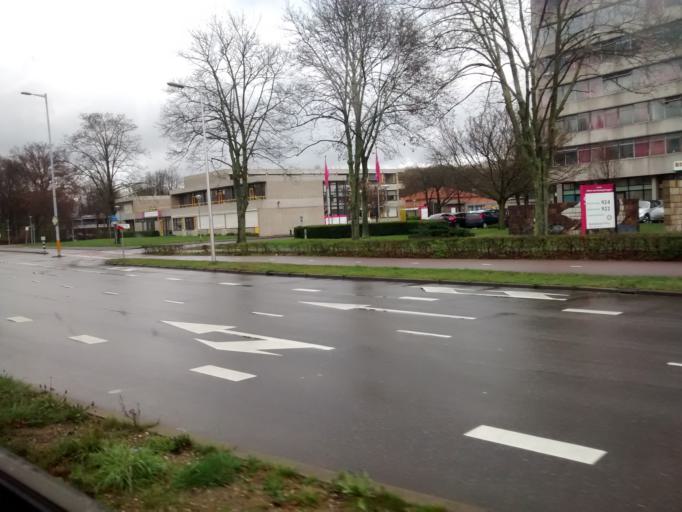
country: NL
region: Utrecht
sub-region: Gemeente Utrecht
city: Utrecht
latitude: 52.0675
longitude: 5.1035
